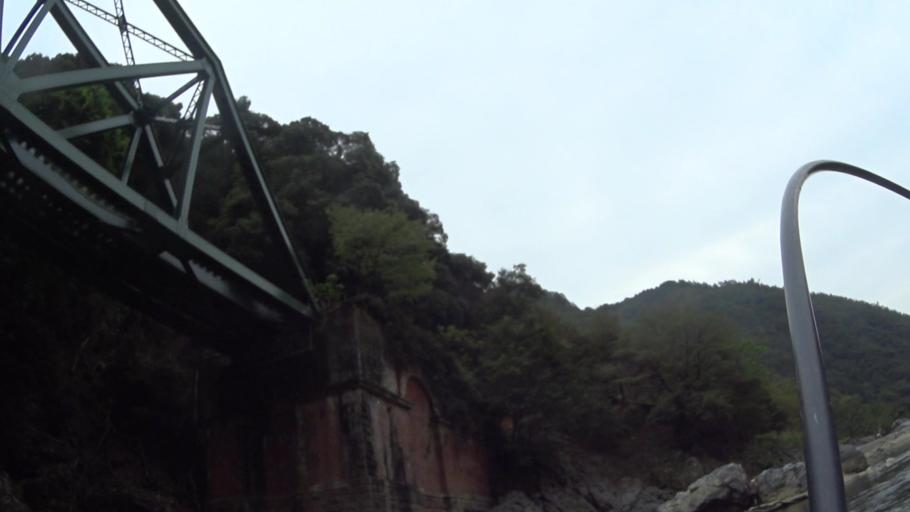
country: JP
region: Kyoto
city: Kameoka
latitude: 35.0270
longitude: 135.6533
